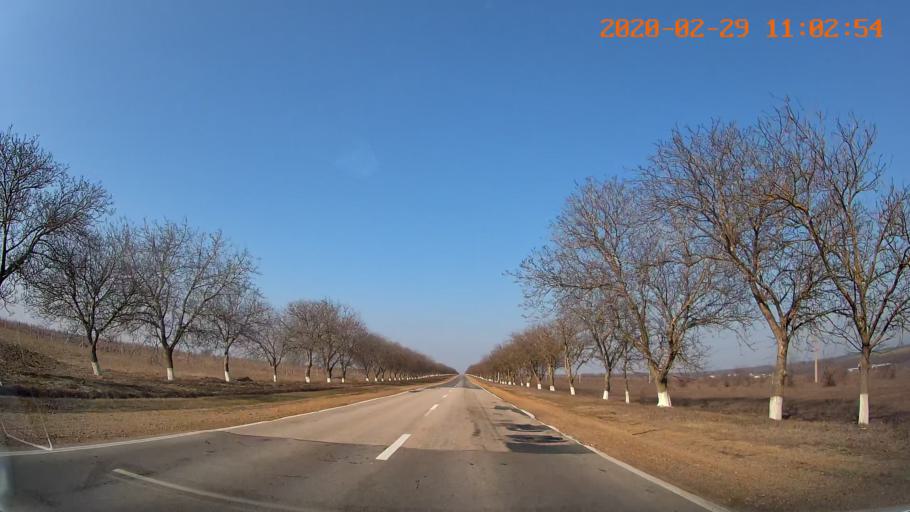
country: MD
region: Telenesti
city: Grigoriopol
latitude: 47.1757
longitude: 29.2288
